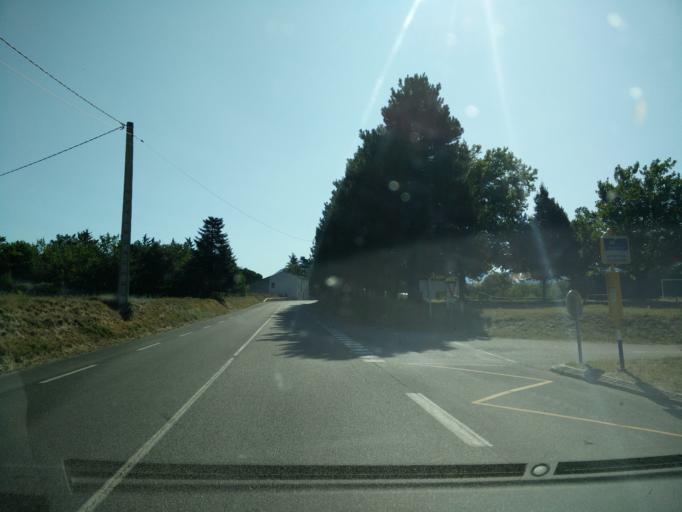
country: FR
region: Rhone-Alpes
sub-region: Departement de la Drome
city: Dieulefit
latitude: 44.5296
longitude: 5.0225
